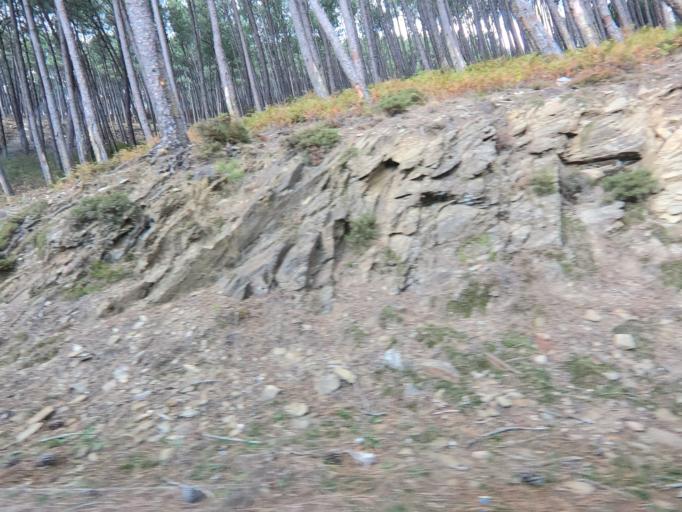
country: PT
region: Vila Real
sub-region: Mondim de Basto
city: Mondim de Basto
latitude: 41.3686
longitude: -7.8452
